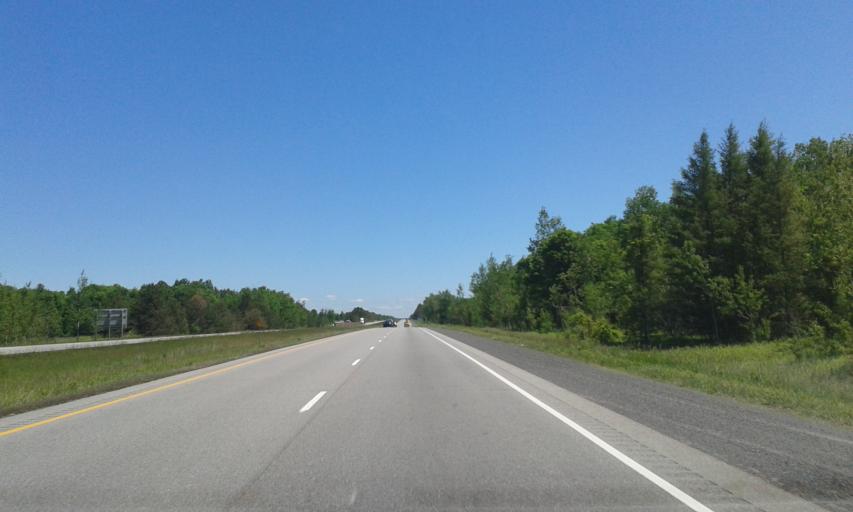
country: US
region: New York
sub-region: St. Lawrence County
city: Ogdensburg
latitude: 44.7958
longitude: -75.4286
